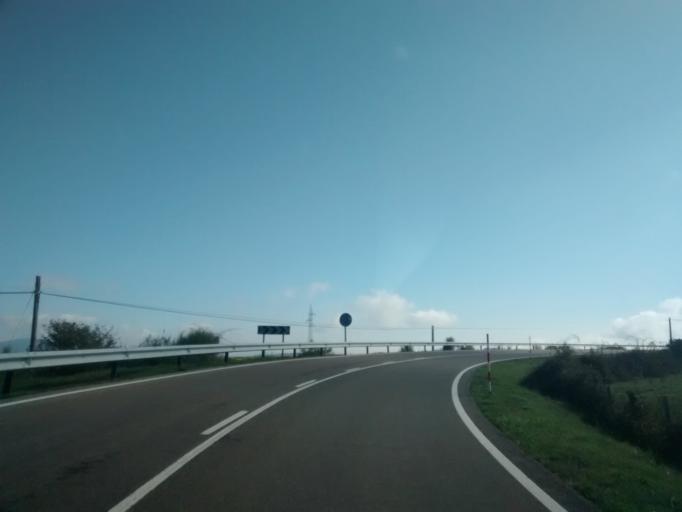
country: ES
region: Cantabria
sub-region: Provincia de Cantabria
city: Reinosa
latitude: 42.9706
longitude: -4.0725
